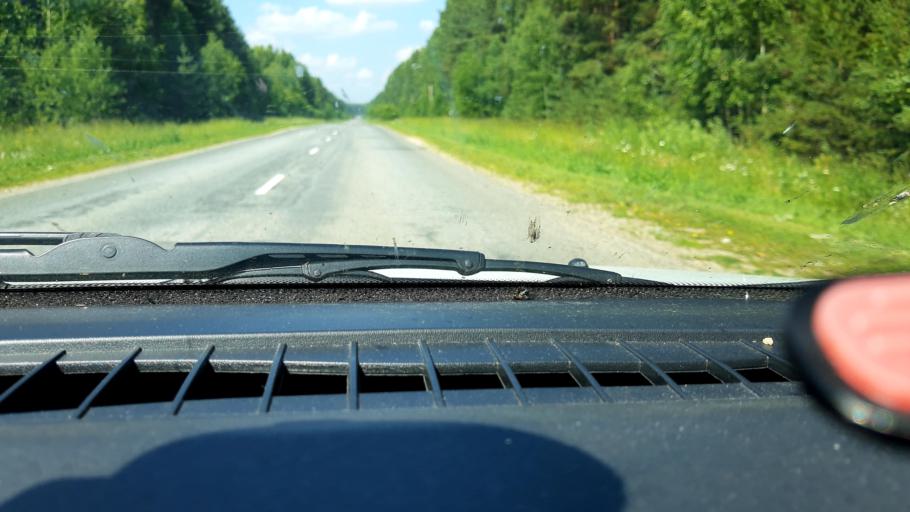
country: RU
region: Nizjnij Novgorod
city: Tonkino
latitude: 57.2842
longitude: 46.4618
